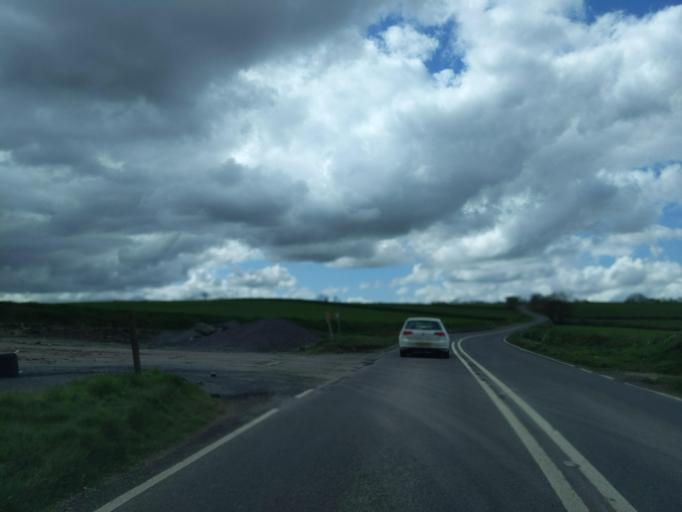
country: GB
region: England
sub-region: Cornwall
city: Callington
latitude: 50.4854
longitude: -4.3569
